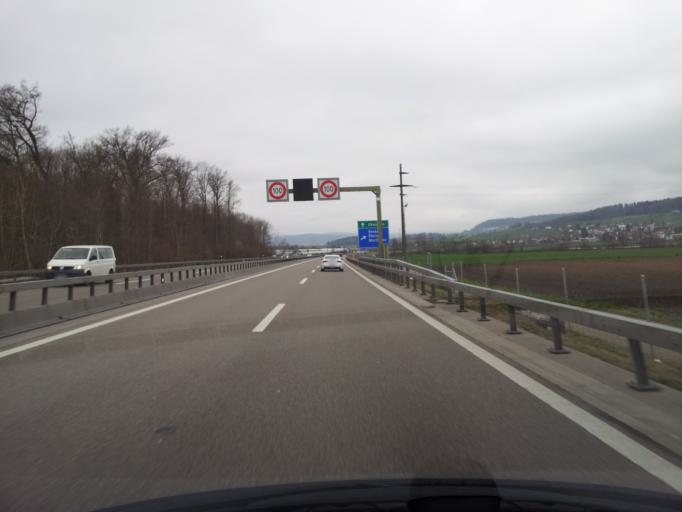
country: CH
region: Zurich
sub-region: Bezirk Andelfingen
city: Marthalen
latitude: 47.6396
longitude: 8.6573
